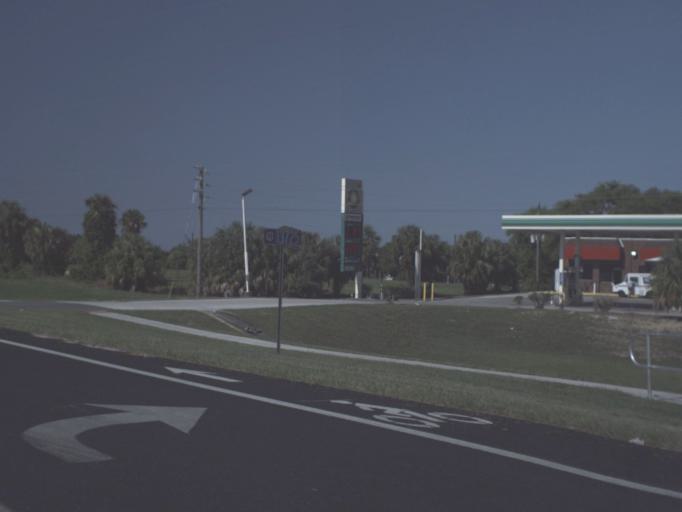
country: US
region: Florida
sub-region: Pasco County
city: Hudson
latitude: 28.3568
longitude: -82.6985
